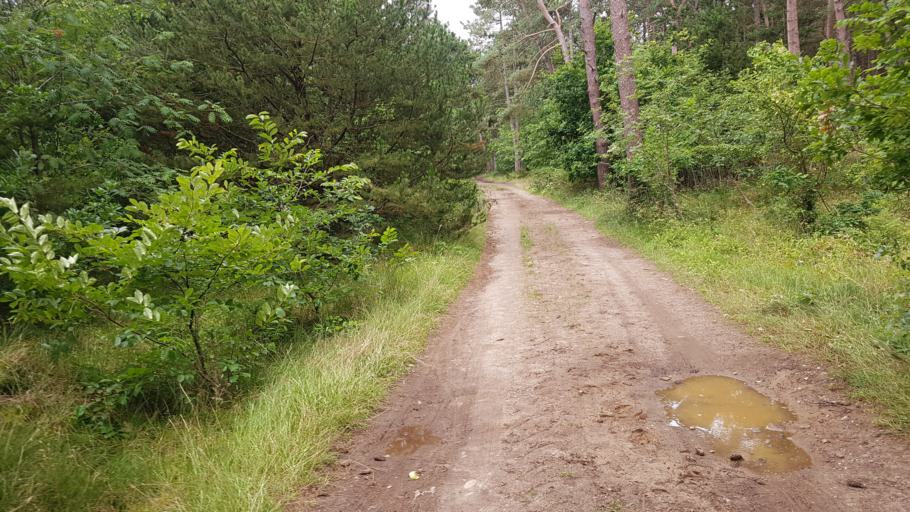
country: DE
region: Schleswig-Holstein
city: List
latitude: 55.0992
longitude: 8.5295
